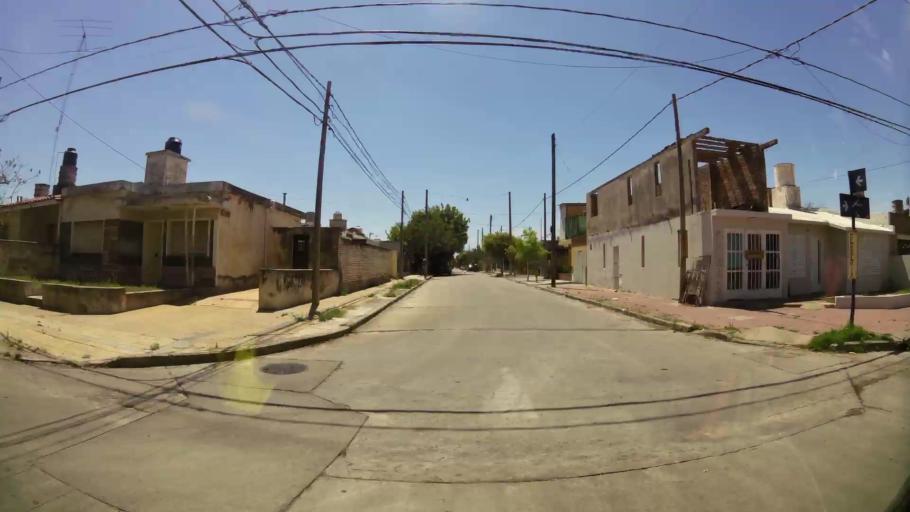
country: AR
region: Cordoba
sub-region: Departamento de Capital
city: Cordoba
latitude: -31.3819
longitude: -64.1586
